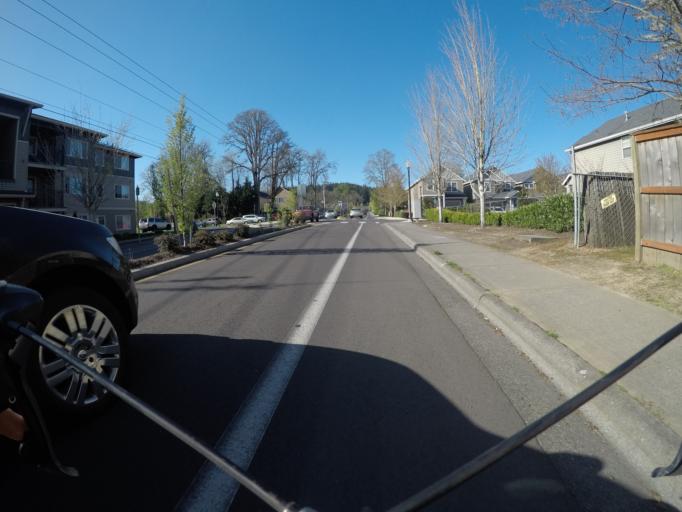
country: US
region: Oregon
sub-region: Washington County
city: King City
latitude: 45.3978
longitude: -122.8119
